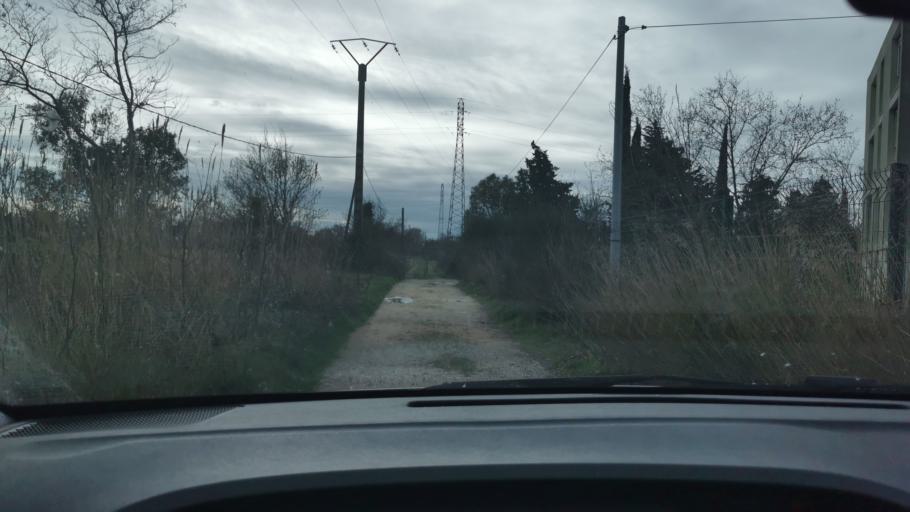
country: FR
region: Provence-Alpes-Cote d'Azur
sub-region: Departement des Bouches-du-Rhone
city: Miramas
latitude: 43.5778
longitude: 4.9901
